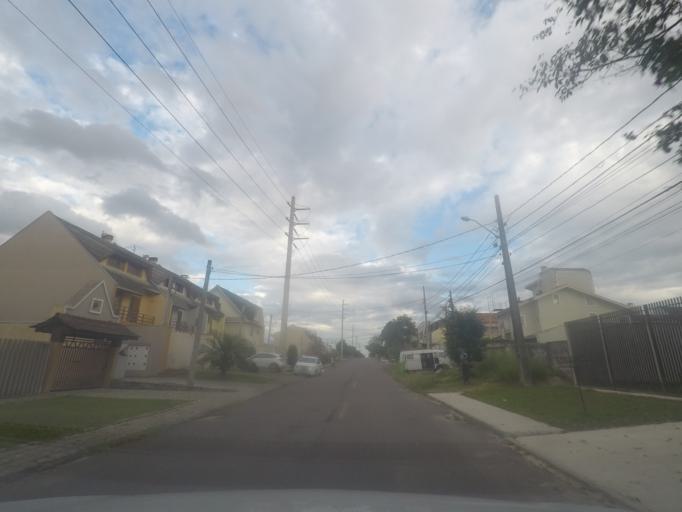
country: BR
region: Parana
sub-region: Pinhais
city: Pinhais
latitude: -25.4605
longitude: -49.2219
